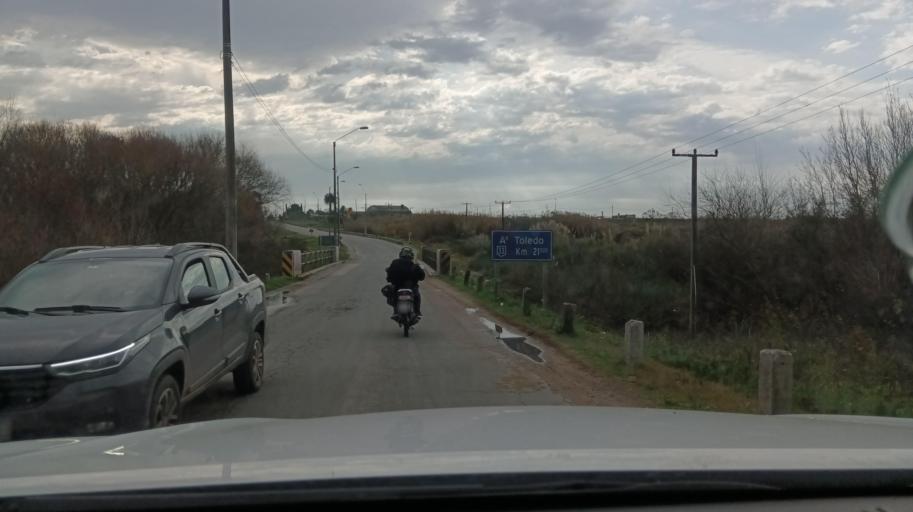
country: UY
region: Canelones
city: Toledo
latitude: -34.7517
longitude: -56.1088
